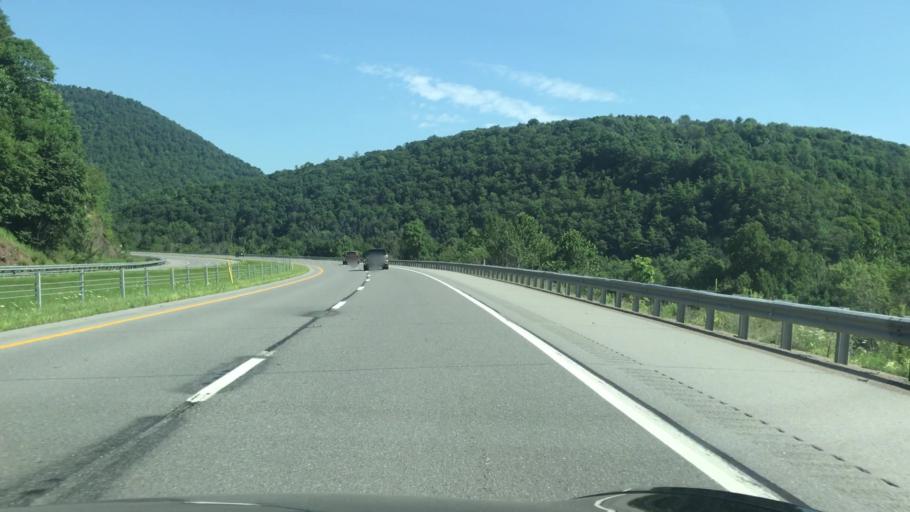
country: US
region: Pennsylvania
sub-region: Lycoming County
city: Garden View
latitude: 41.3406
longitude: -77.0891
